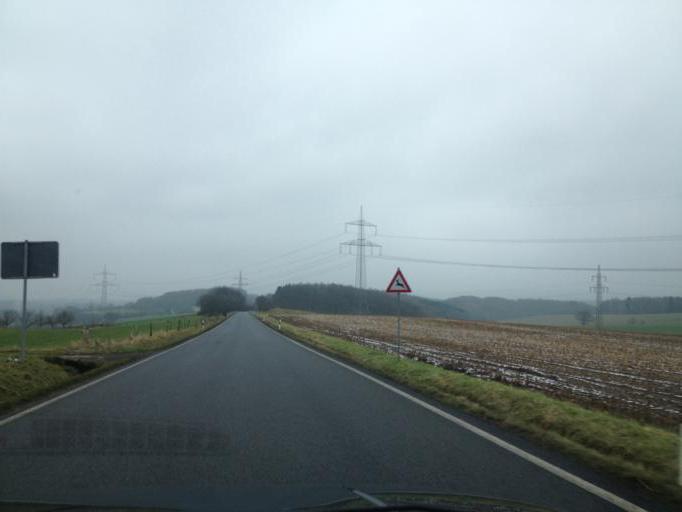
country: DE
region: Rheinland-Pfalz
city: Dunzweiler
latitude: 49.3863
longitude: 7.3004
